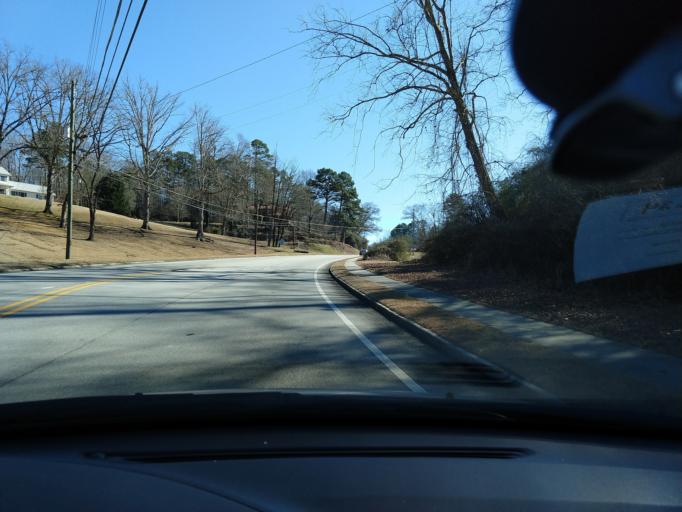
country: US
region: Georgia
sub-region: Stephens County
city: Toccoa
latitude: 34.5927
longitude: -83.3443
